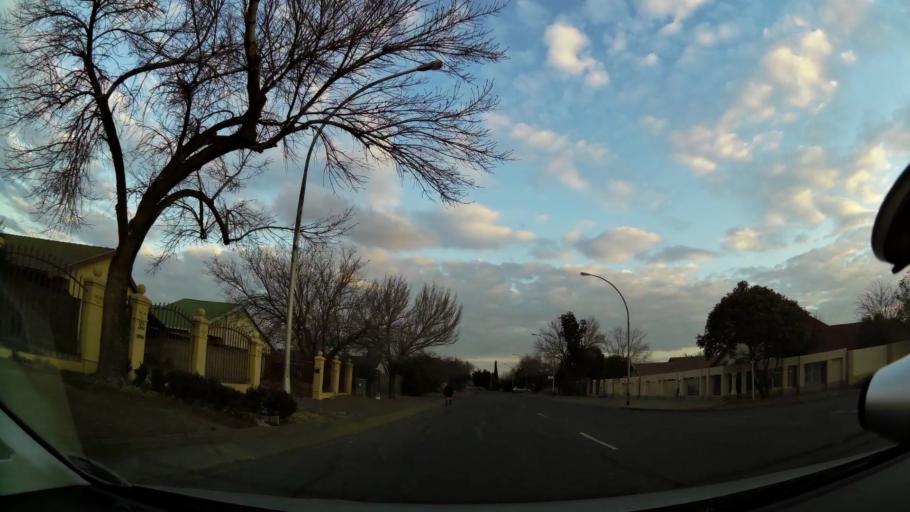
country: ZA
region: Orange Free State
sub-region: Mangaung Metropolitan Municipality
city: Bloemfontein
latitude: -29.1658
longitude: 26.1848
